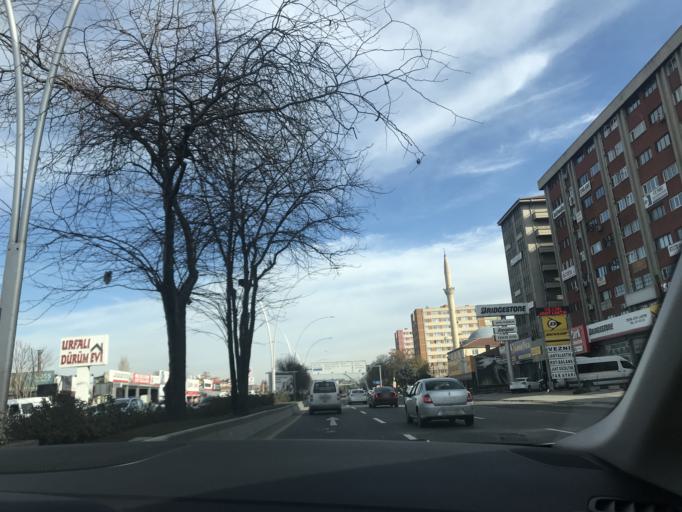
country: TR
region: Ankara
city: Ankara
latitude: 39.9554
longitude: 32.8434
